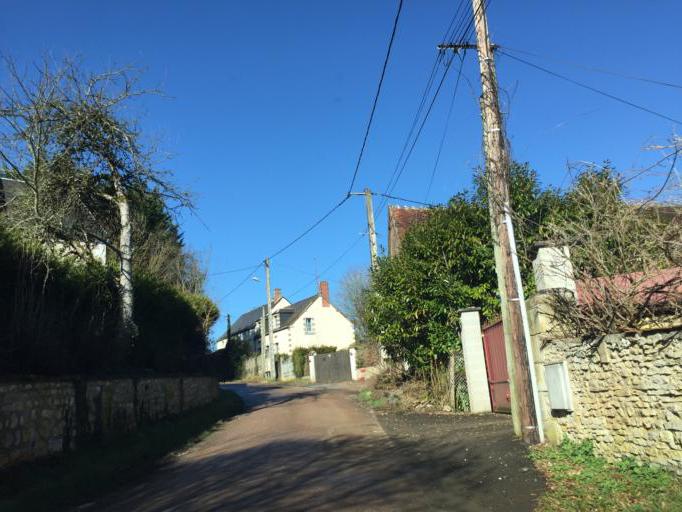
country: FR
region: Bourgogne
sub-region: Departement de l'Yonne
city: Fontenailles
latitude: 47.5448
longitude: 3.3339
